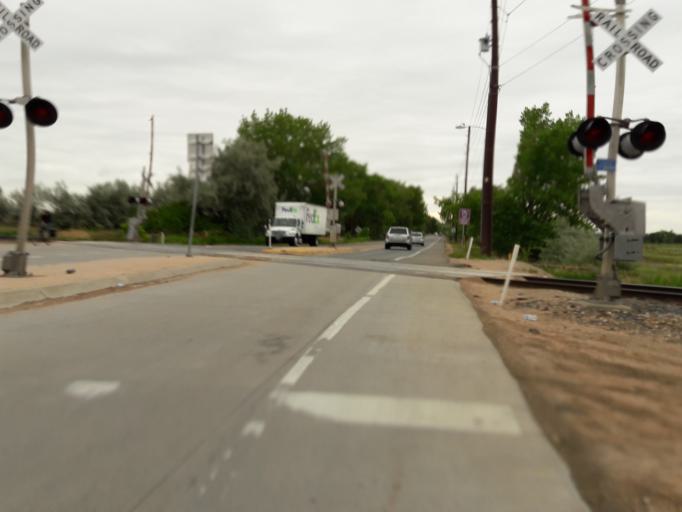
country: US
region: Colorado
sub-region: Boulder County
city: Boulder
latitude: 40.0510
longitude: -105.2327
